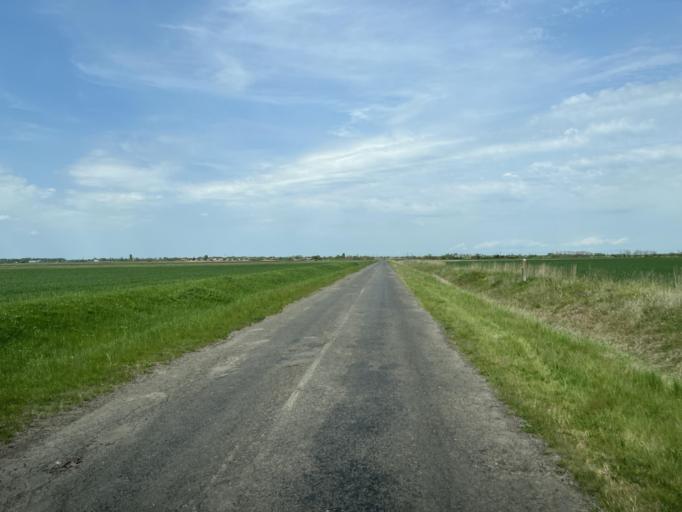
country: HU
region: Pest
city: Tapiogyorgye
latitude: 47.3125
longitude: 19.9724
